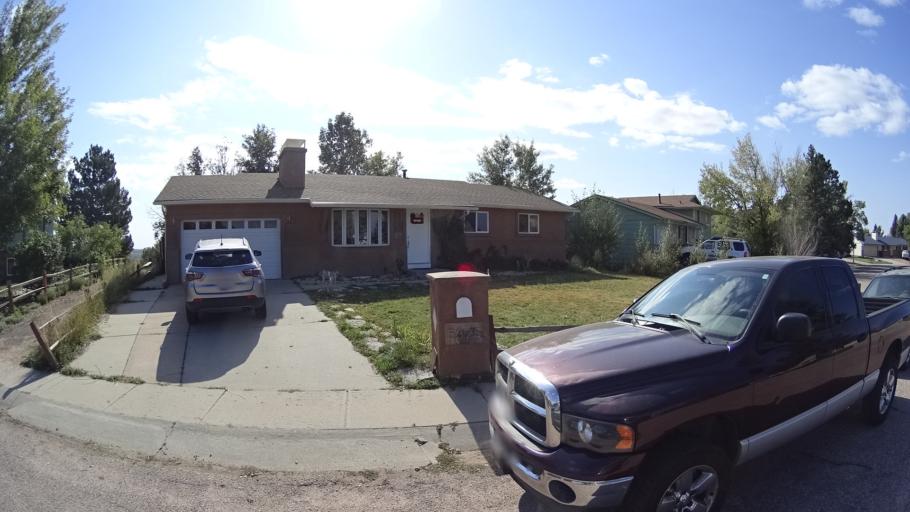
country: US
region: Colorado
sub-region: El Paso County
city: Cimarron Hills
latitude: 38.8834
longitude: -104.7281
